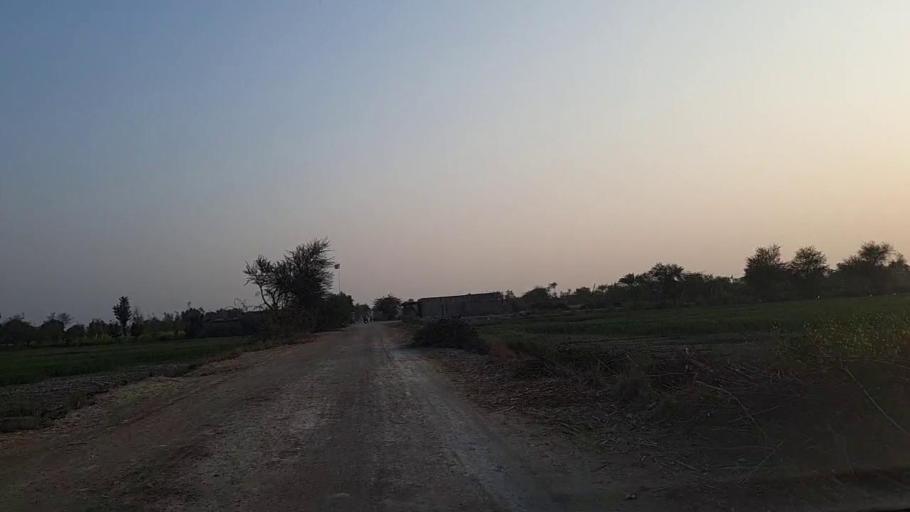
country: PK
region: Sindh
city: Daur
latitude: 26.4179
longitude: 68.3677
